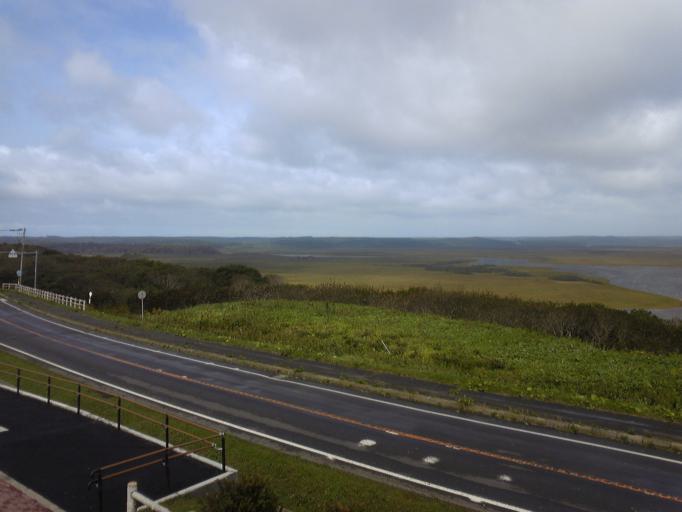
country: JP
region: Hokkaido
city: Nemuro
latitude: 43.0453
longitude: 145.0695
